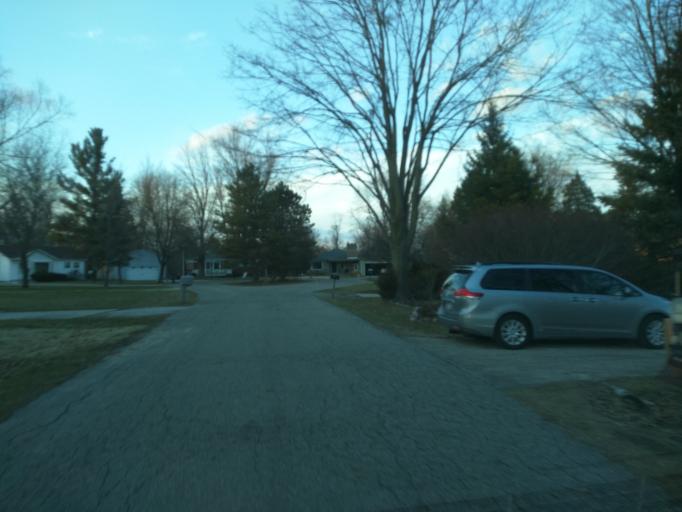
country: US
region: Michigan
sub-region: Ingham County
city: Edgemont Park
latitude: 42.7592
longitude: -84.5822
